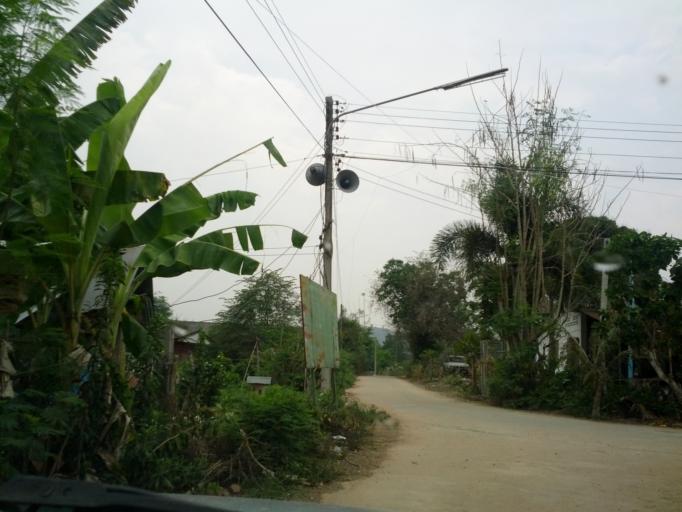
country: TH
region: Chiang Mai
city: Mae Taeng
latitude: 19.1052
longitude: 98.9942
